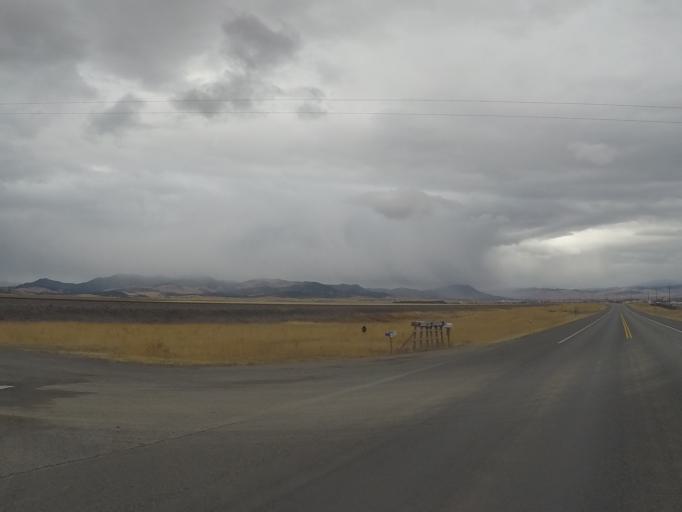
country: US
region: Montana
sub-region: Lewis and Clark County
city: East Helena
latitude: 46.5865
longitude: -111.8723
